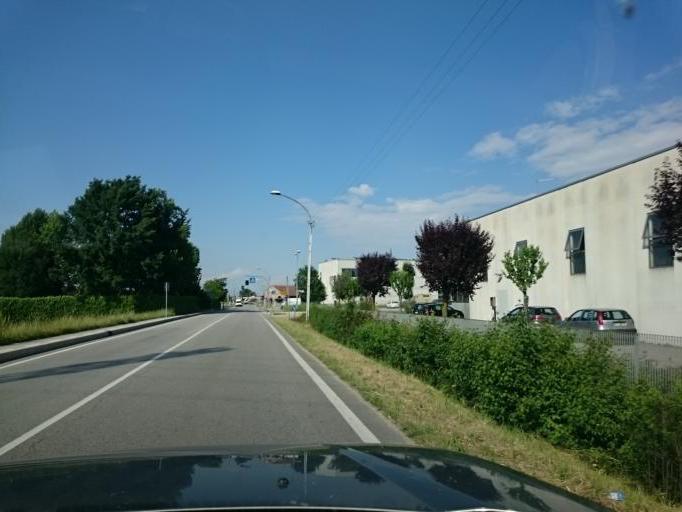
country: IT
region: Veneto
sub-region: Provincia di Vicenza
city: Montegalda
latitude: 45.4574
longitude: 11.6895
